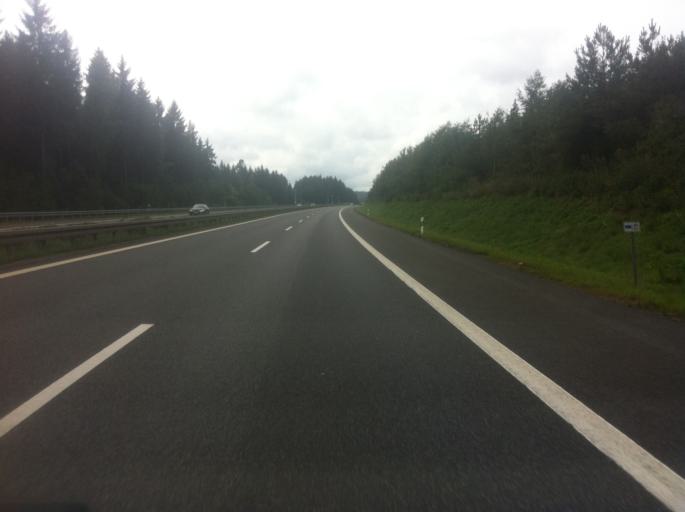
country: DE
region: Bavaria
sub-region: Upper Palatinate
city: Pleystein
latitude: 49.6291
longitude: 12.4461
